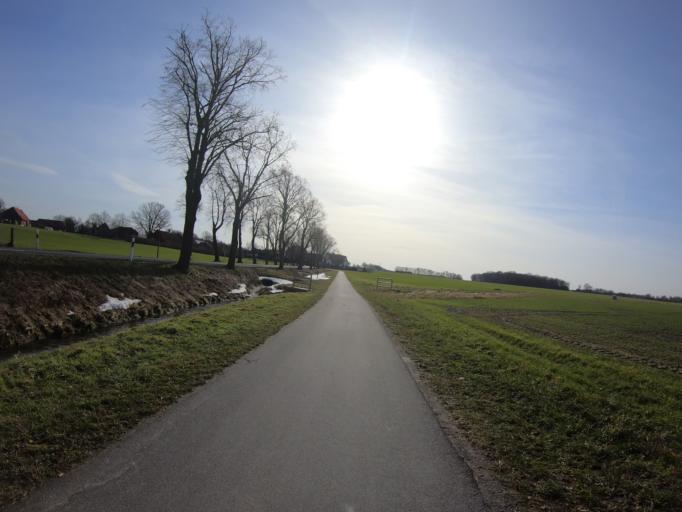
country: DE
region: Lower Saxony
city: Meine
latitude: 52.4056
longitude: 10.5625
